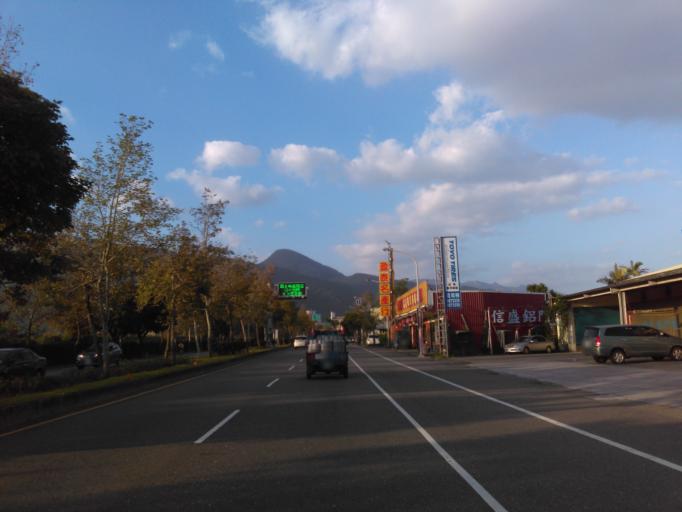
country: TW
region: Taiwan
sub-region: Yilan
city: Yilan
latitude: 24.8131
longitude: 121.7675
